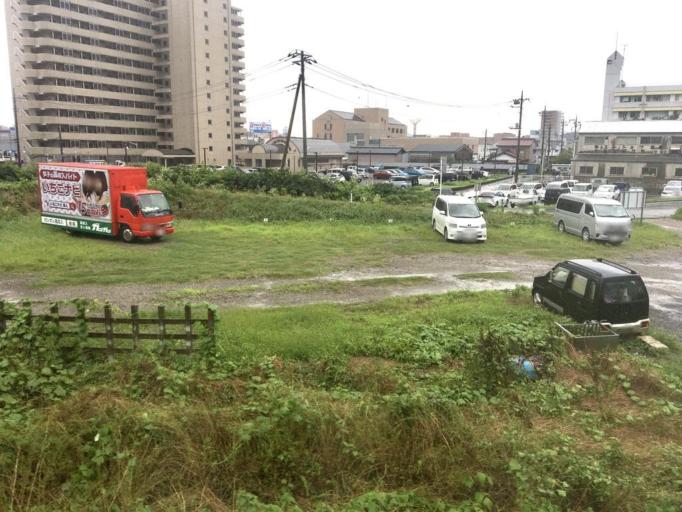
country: JP
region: Tochigi
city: Ashikaga
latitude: 36.3234
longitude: 139.4532
